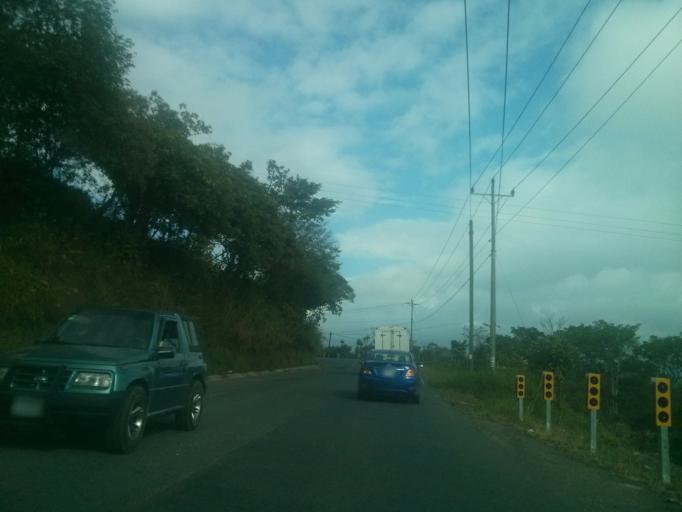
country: CR
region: Cartago
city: Paraiso
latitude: 9.8607
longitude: -83.8395
